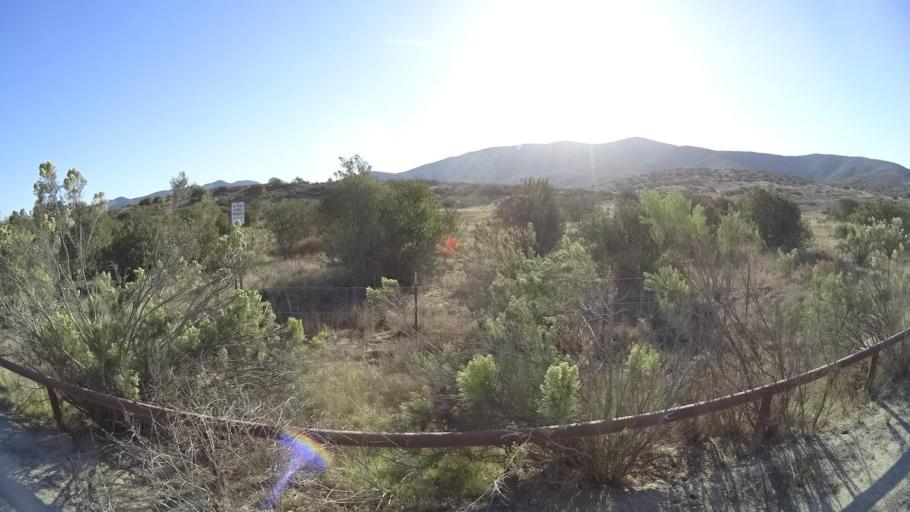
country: US
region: California
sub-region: San Diego County
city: Jamul
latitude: 32.6655
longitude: -116.9279
